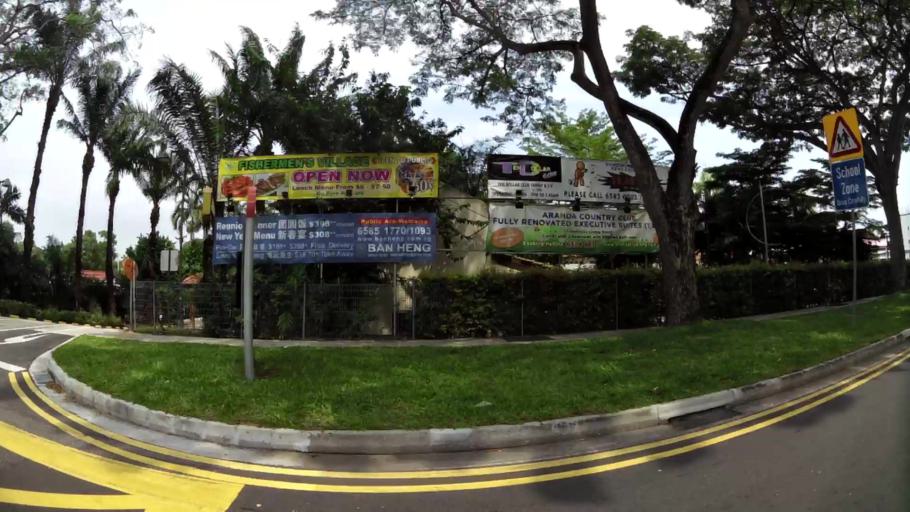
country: MY
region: Johor
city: Kampung Pasir Gudang Baru
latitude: 1.3752
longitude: 103.9534
